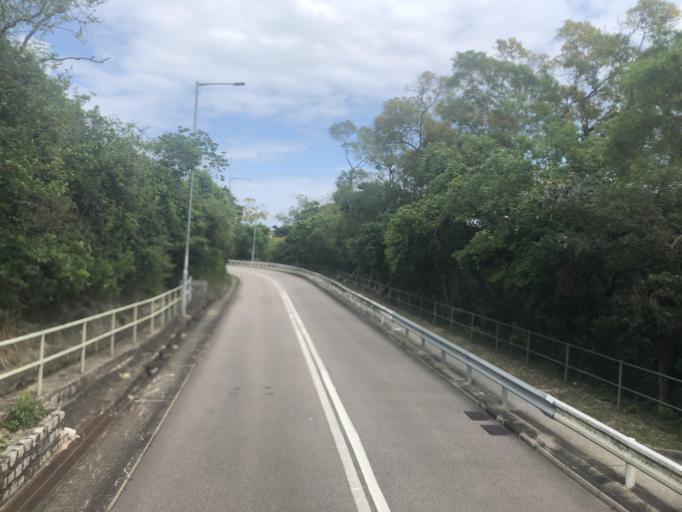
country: HK
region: Sai Kung
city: Sai Kung
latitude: 22.3867
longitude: 114.3039
